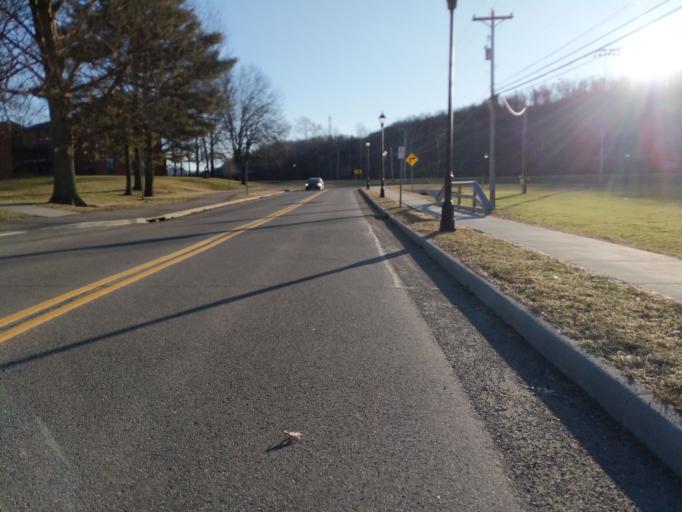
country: US
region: Ohio
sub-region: Athens County
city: Athens
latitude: 39.3293
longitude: -82.0907
